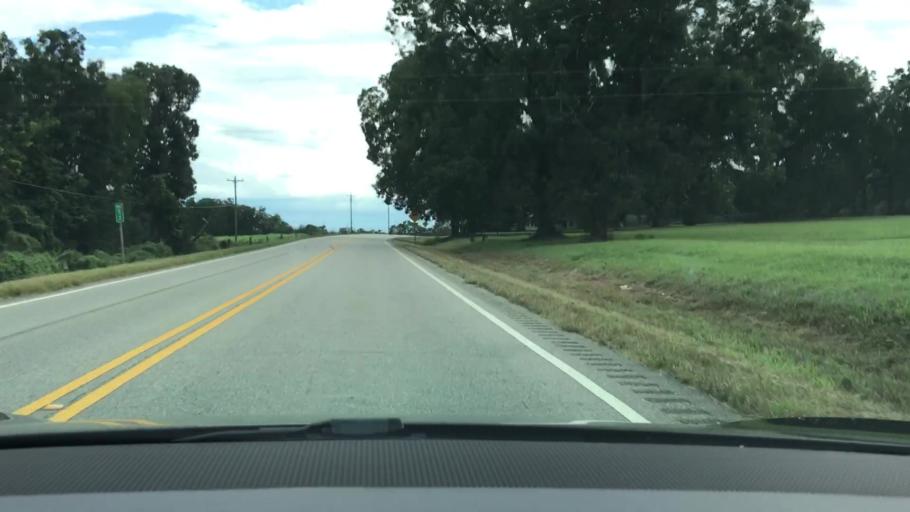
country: US
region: Alabama
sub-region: Pike County
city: Troy
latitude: 31.6641
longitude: -85.9594
